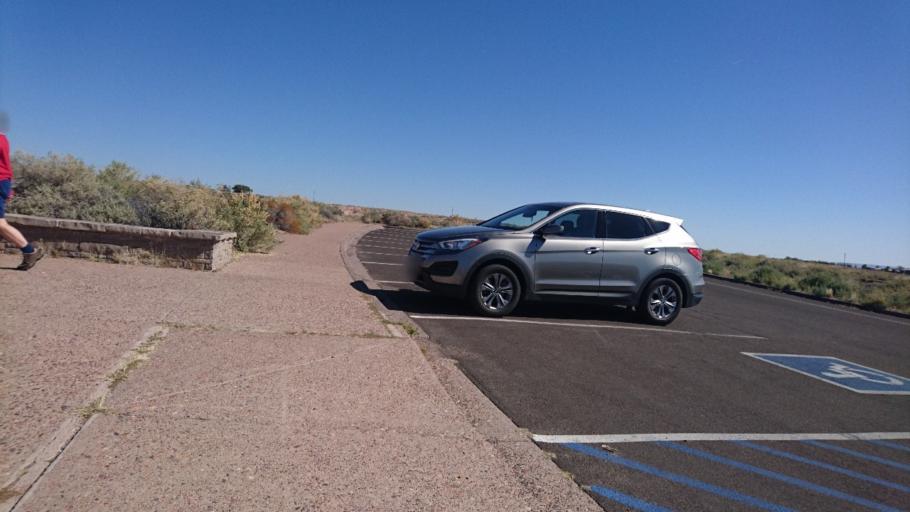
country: US
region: Arizona
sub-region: Navajo County
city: Holbrook
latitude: 35.0689
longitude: -109.7946
